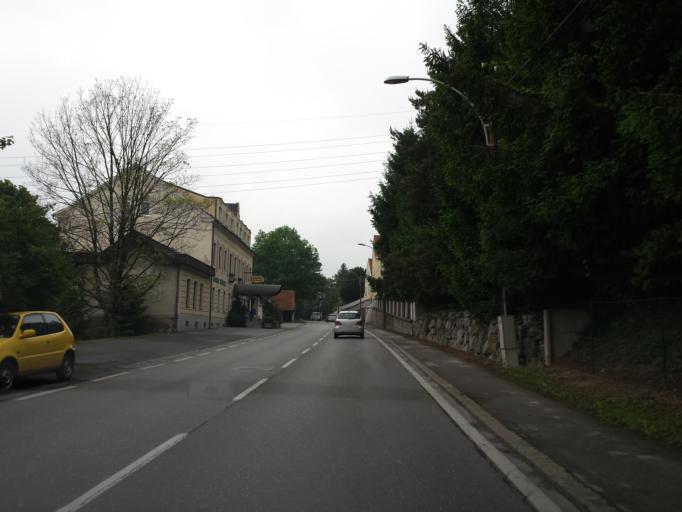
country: AT
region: Styria
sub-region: Graz Stadt
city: Goesting
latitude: 47.0966
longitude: 15.4236
